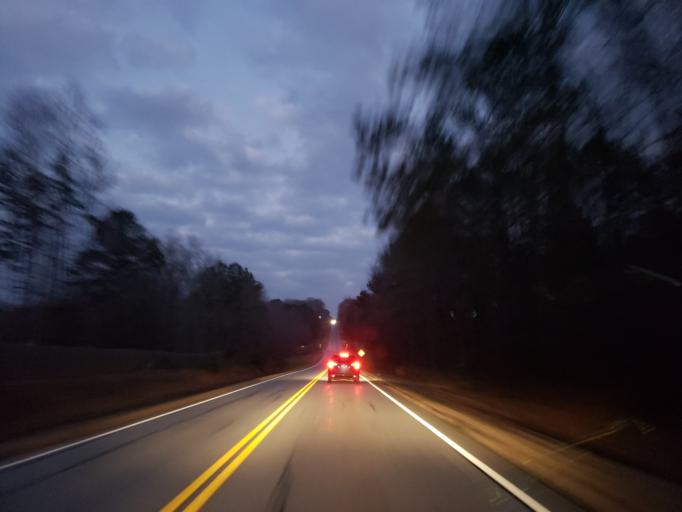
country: US
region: Georgia
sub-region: Carroll County
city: Temple
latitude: 33.8360
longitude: -85.0099
